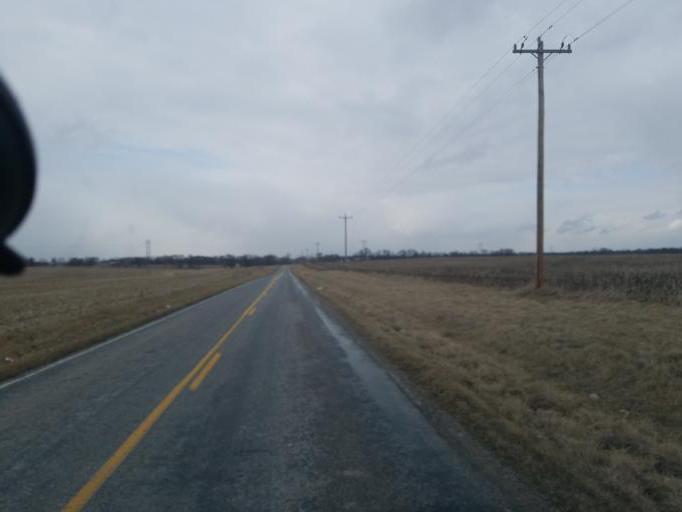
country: US
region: Missouri
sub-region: Boone County
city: Hallsville
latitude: 39.2472
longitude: -92.2928
